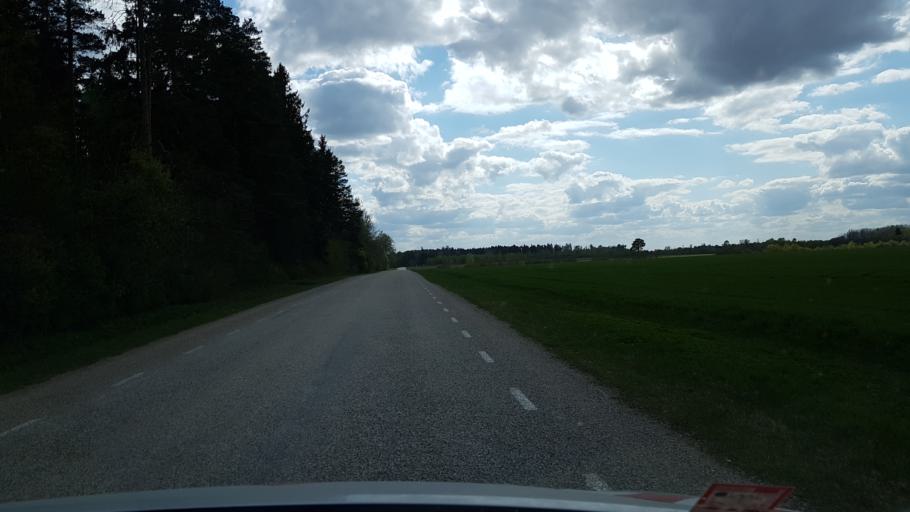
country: EE
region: Tartu
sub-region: Tartu linn
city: Tartu
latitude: 58.3538
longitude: 26.8535
